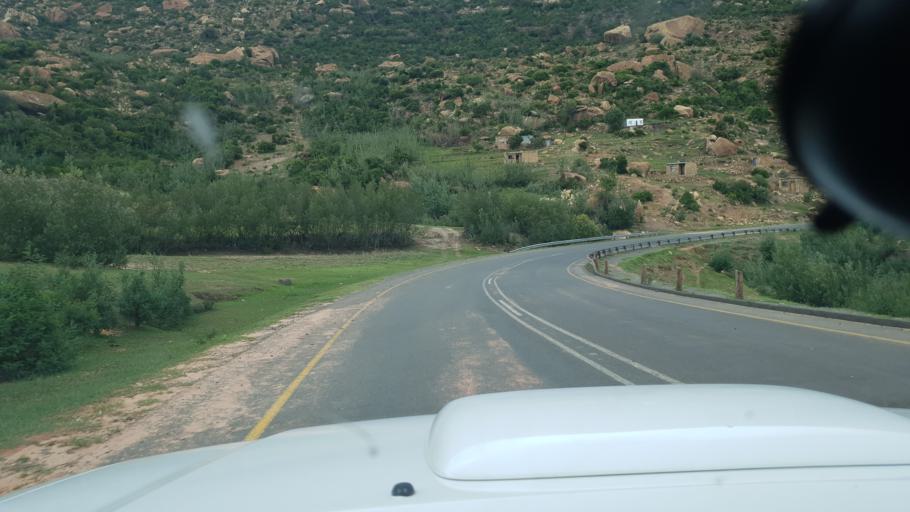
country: LS
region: Maseru
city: Maseru
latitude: -29.4653
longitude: 27.4966
